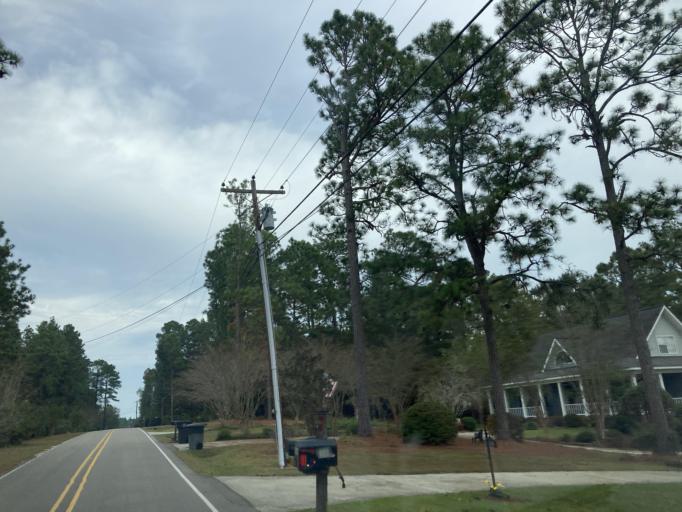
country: US
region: Mississippi
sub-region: Lamar County
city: West Hattiesburg
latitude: 31.3117
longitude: -89.4389
